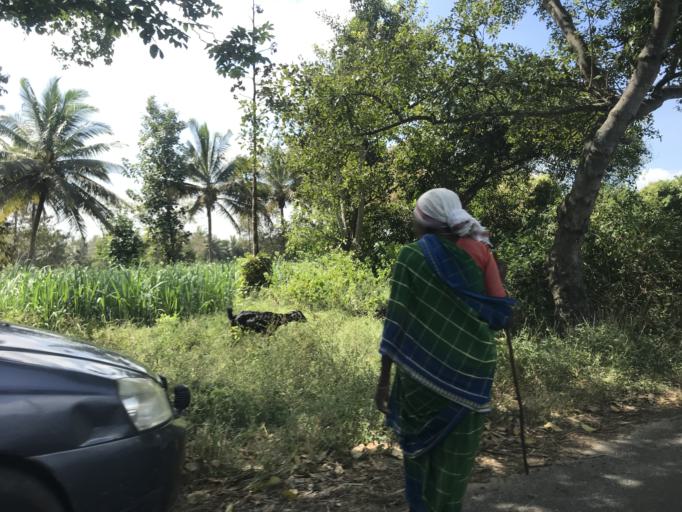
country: IN
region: Karnataka
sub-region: Mandya
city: Shrirangapattana
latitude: 12.4209
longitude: 76.6578
